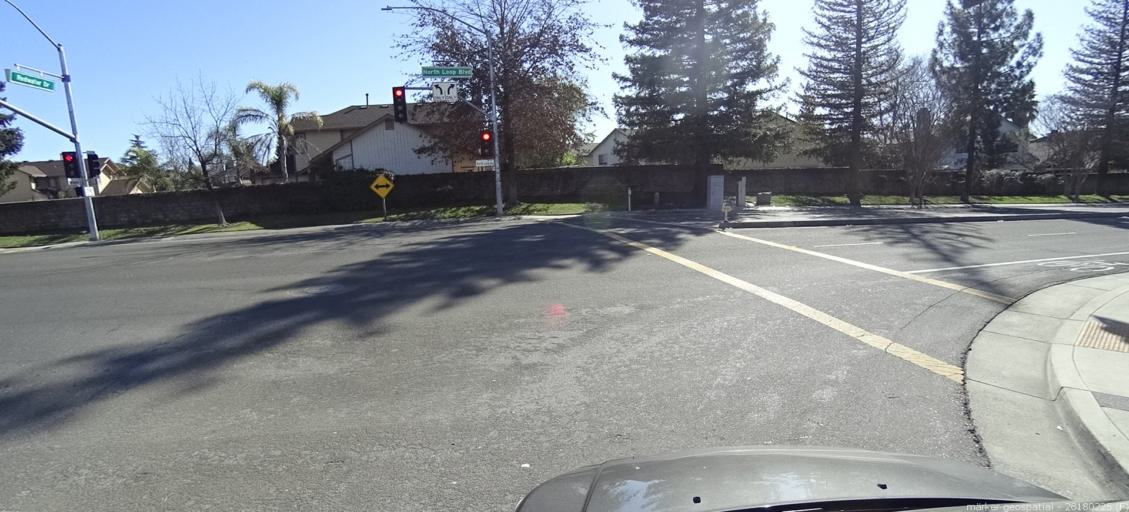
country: US
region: California
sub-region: Sacramento County
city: North Highlands
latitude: 38.7217
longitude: -121.3690
